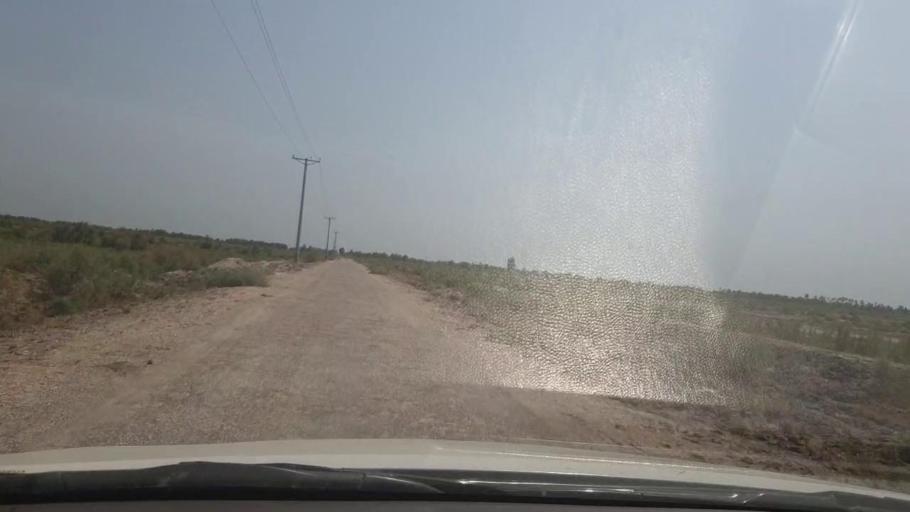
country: PK
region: Sindh
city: Garhi Yasin
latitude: 27.9848
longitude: 68.5021
